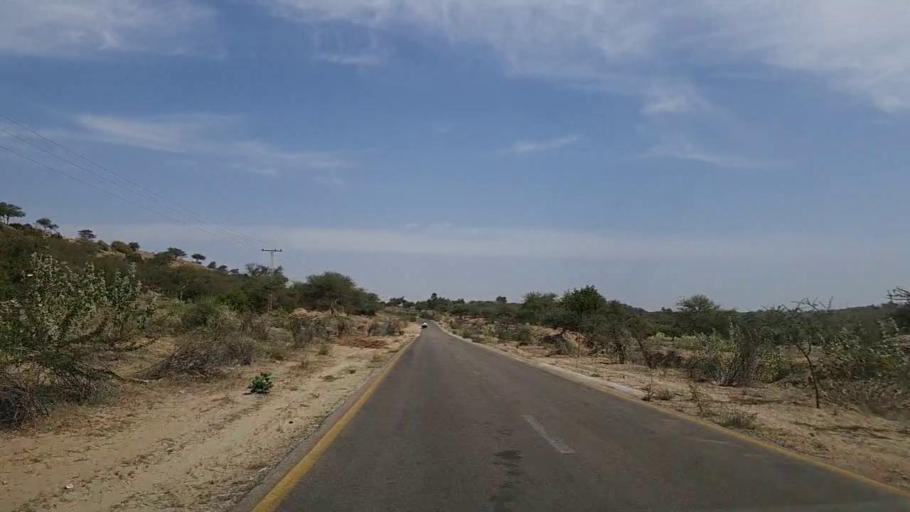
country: PK
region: Sindh
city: Mithi
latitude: 24.7775
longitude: 69.8071
